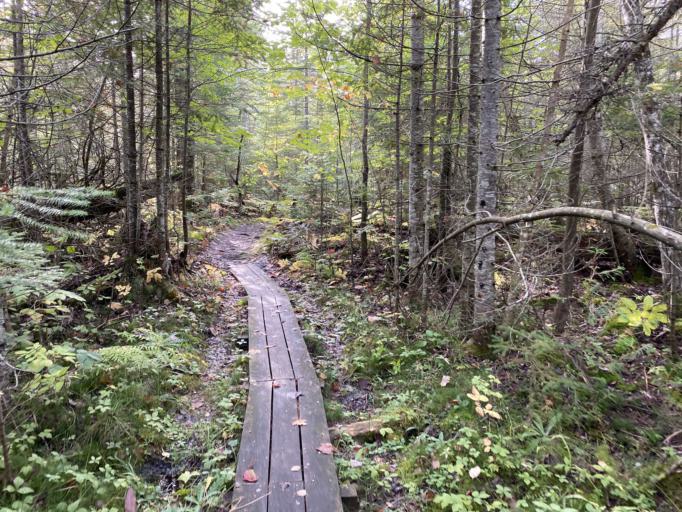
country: US
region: Michigan
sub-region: Mackinac County
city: Saint Ignace
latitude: 45.7416
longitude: -84.8902
